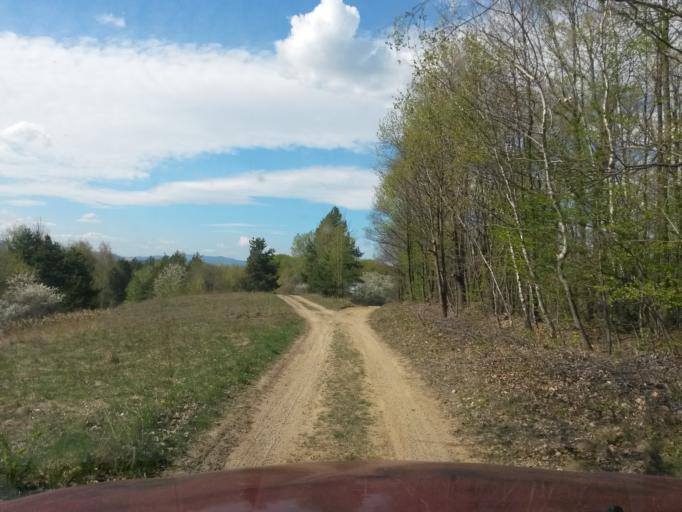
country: SK
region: Presovsky
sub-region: Okres Presov
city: Presov
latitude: 48.9379
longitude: 21.1219
